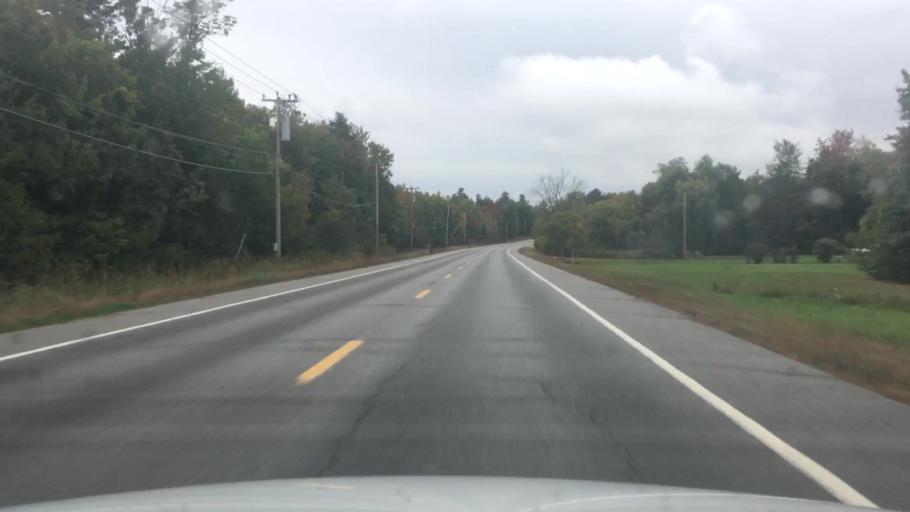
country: US
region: Maine
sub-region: Kennebec County
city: Rome
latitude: 44.5156
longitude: -69.8762
